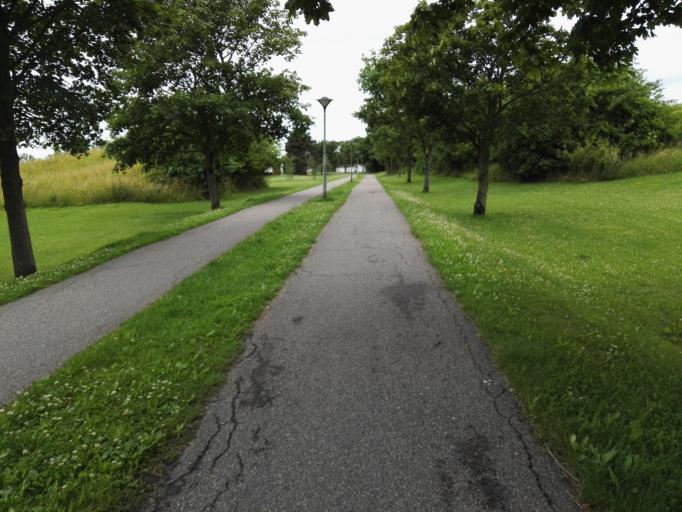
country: DK
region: Capital Region
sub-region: Egedal Kommune
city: Olstykke
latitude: 55.7768
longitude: 12.1675
